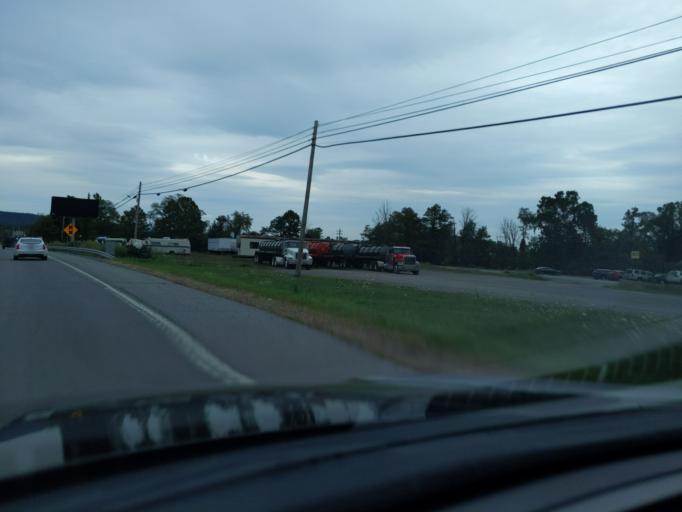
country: US
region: Pennsylvania
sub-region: Blair County
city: Duncansville
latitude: 40.4189
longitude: -78.4386
